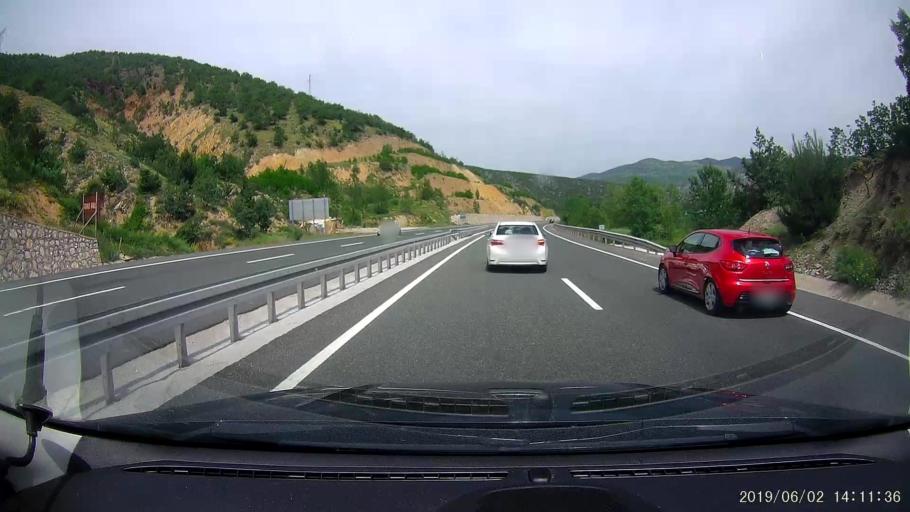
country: TR
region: Cankiri
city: Yaprakli
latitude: 40.9111
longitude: 33.7872
